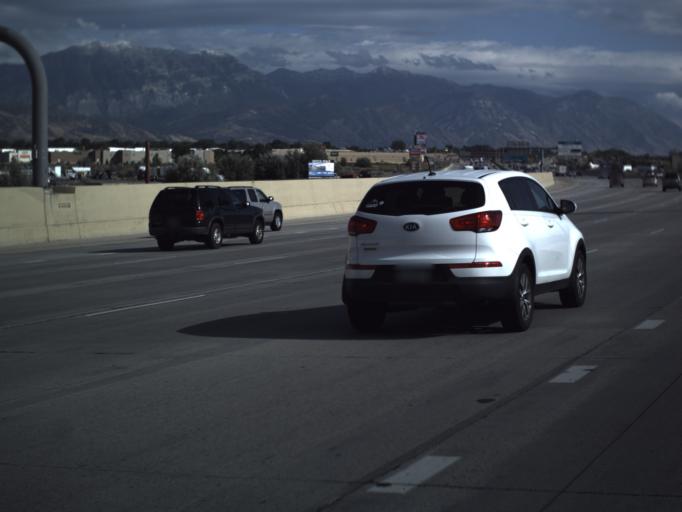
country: US
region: Utah
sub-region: Utah County
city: Lehi
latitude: 40.3848
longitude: -111.8319
